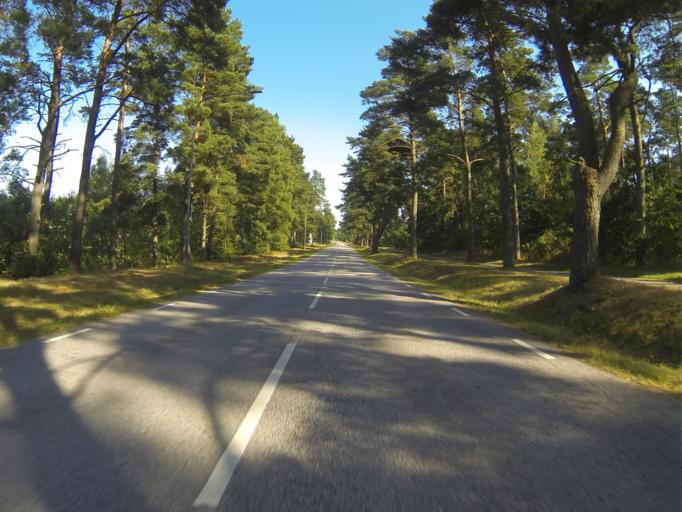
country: SE
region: Skane
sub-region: Hoors Kommun
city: Loberod
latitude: 55.7192
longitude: 13.4837
